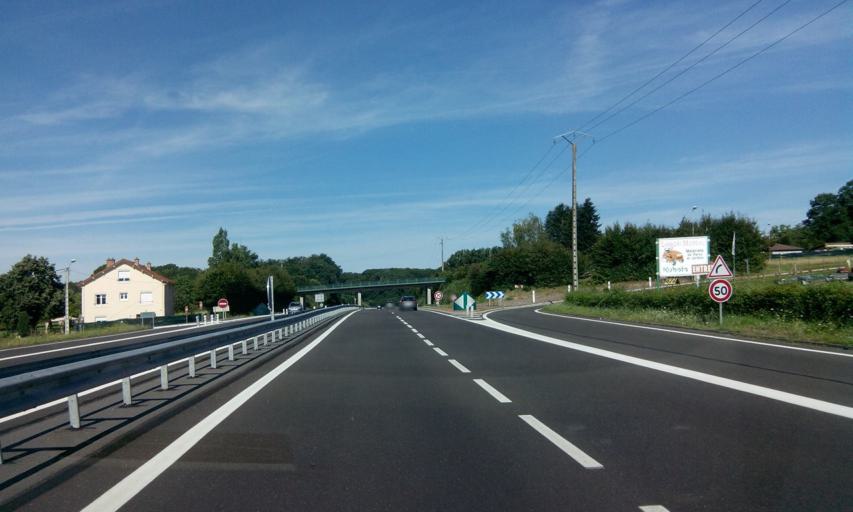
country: FR
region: Limousin
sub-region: Departement de la Haute-Vienne
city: Isle
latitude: 45.8371
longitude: 1.1957
